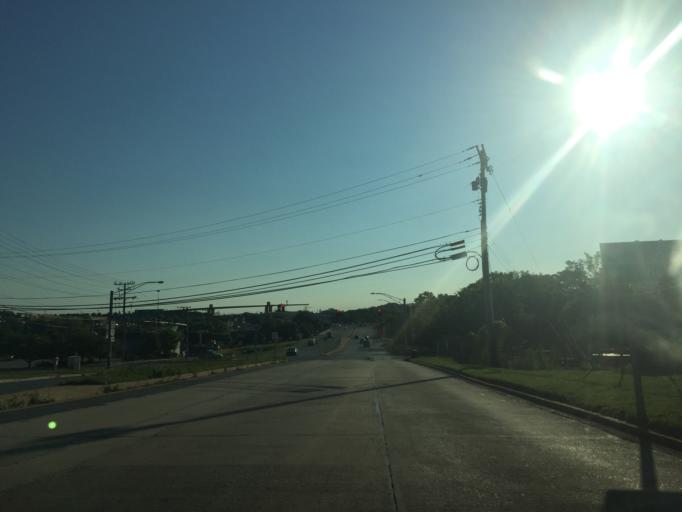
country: US
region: Maryland
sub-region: Baltimore County
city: Lansdowne
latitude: 39.2430
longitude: -76.6767
